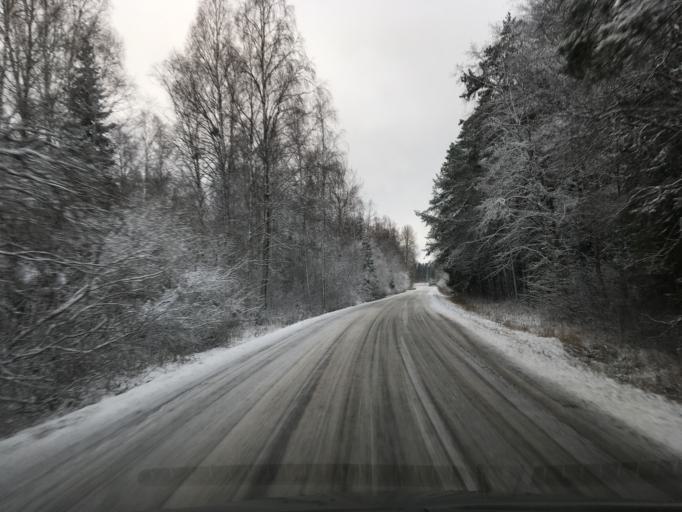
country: EE
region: Harju
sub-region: Raasiku vald
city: Raasiku
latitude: 59.2370
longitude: 25.1713
